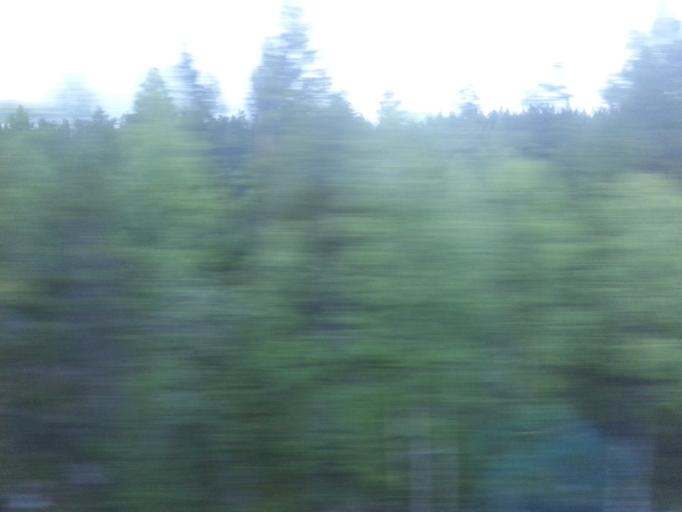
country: NO
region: Oppland
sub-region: Dovre
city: Dombas
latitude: 62.1115
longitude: 9.0891
